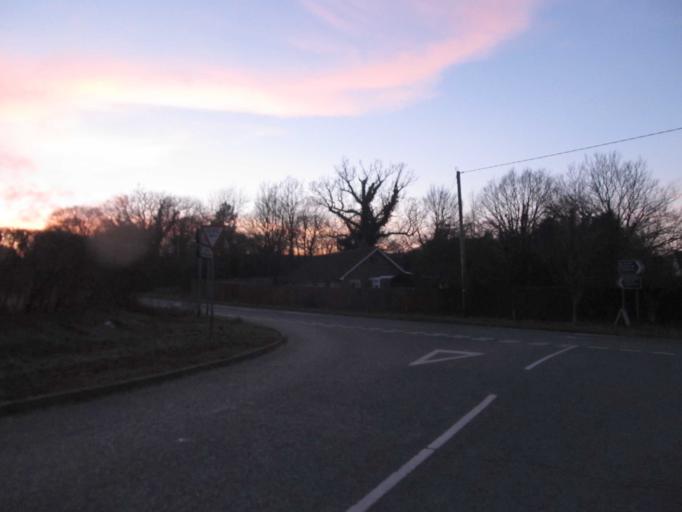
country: GB
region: England
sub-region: West Sussex
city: Petworth
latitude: 50.9889
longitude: -0.6746
